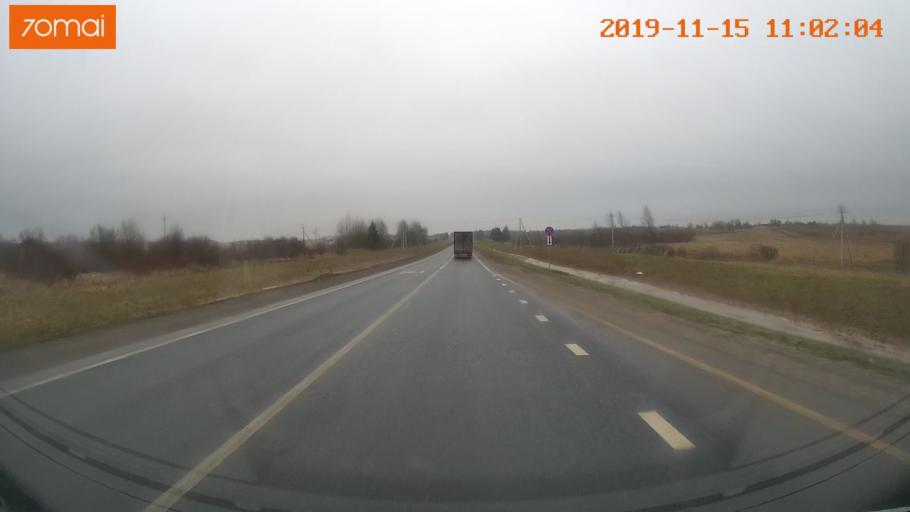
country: RU
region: Vologda
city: Chebsara
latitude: 59.1303
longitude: 38.9327
